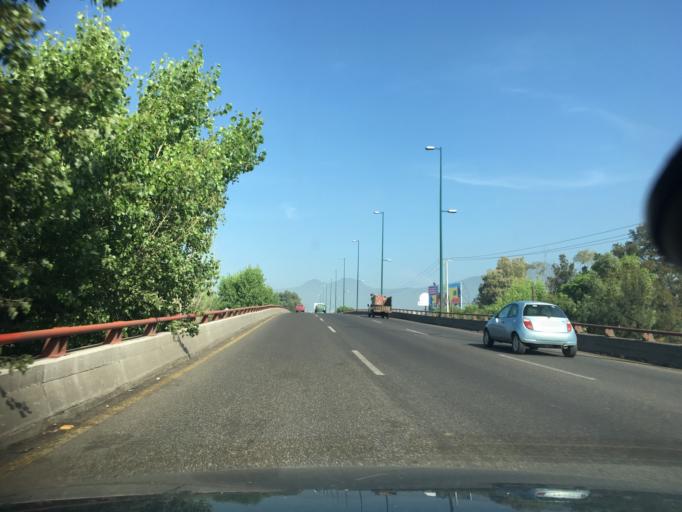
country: MX
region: Michoacan
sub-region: Tarimbaro
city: Real Hacienda (Metropolis)
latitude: 19.7255
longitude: -101.2032
